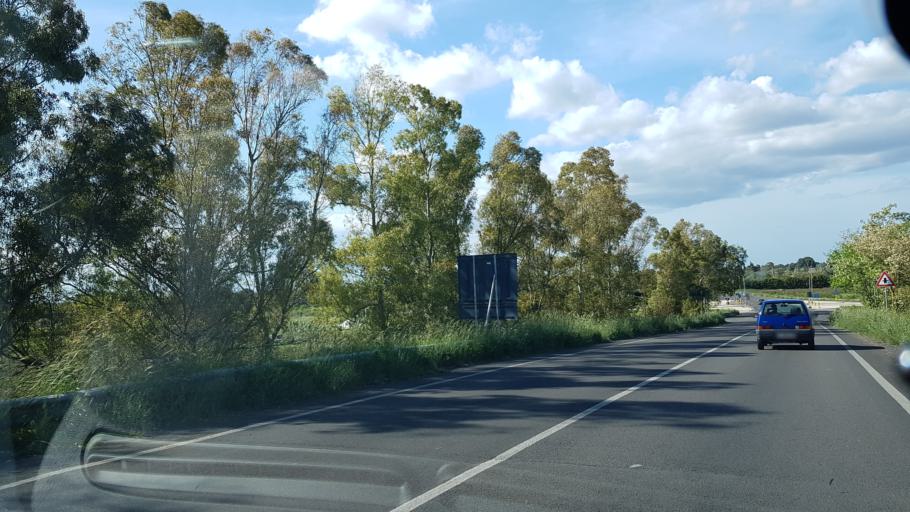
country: IT
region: Apulia
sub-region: Provincia di Brindisi
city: Mesagne
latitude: 40.5605
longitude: 17.7878
